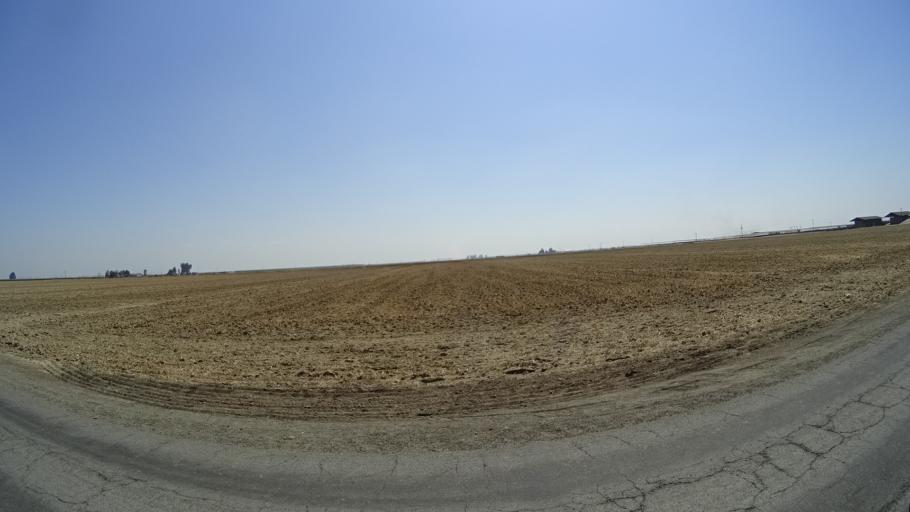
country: US
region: California
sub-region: Tulare County
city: London
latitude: 36.4041
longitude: -119.5289
